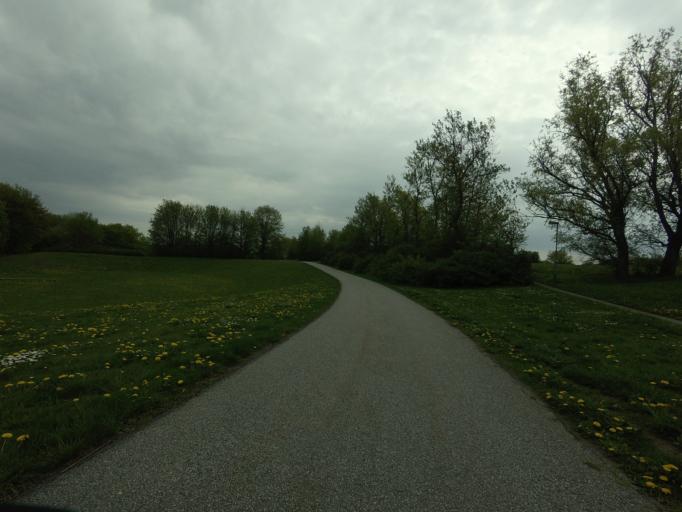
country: SE
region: Skane
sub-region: Malmo
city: Tygelsjo
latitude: 55.5547
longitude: 13.0040
